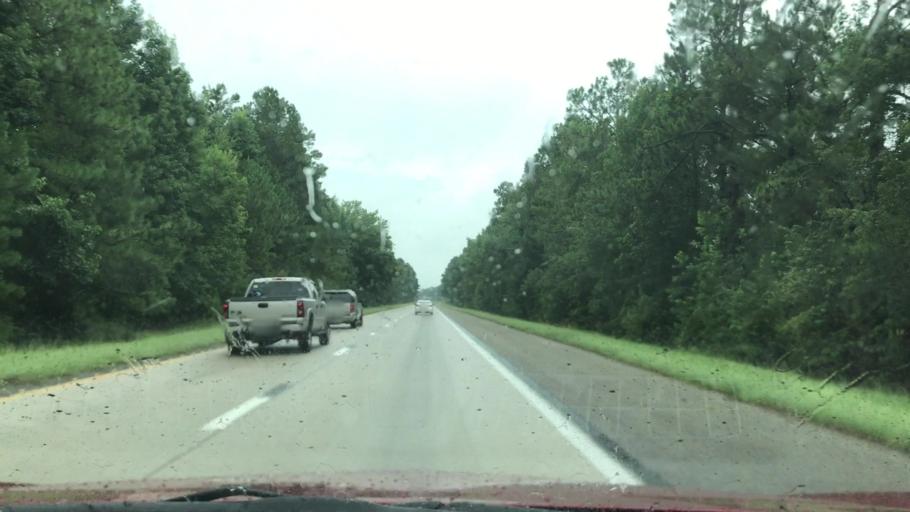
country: US
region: South Carolina
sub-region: Dorchester County
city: Ridgeville
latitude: 33.1947
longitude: -80.3943
